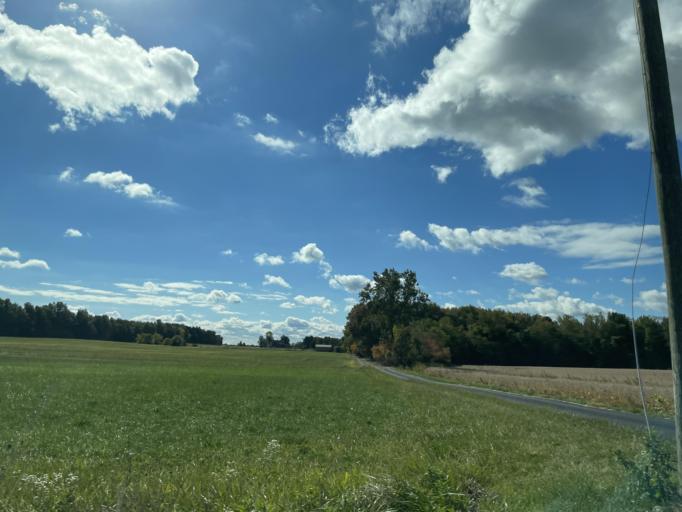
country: US
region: Indiana
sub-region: Allen County
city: Fort Wayne
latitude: 41.1183
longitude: -85.2410
